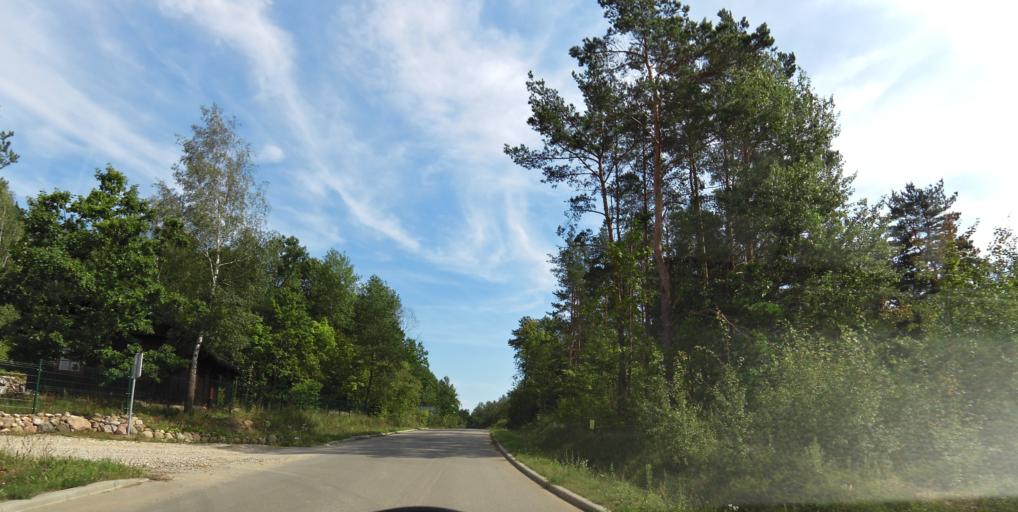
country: LT
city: Grigiskes
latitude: 54.7250
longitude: 25.0764
